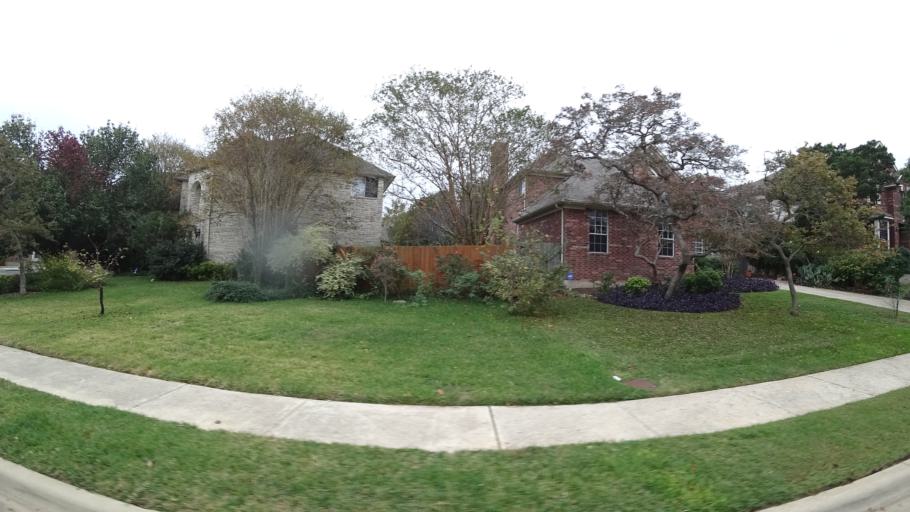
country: US
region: Texas
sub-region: Williamson County
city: Anderson Mill
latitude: 30.4386
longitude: -97.8167
